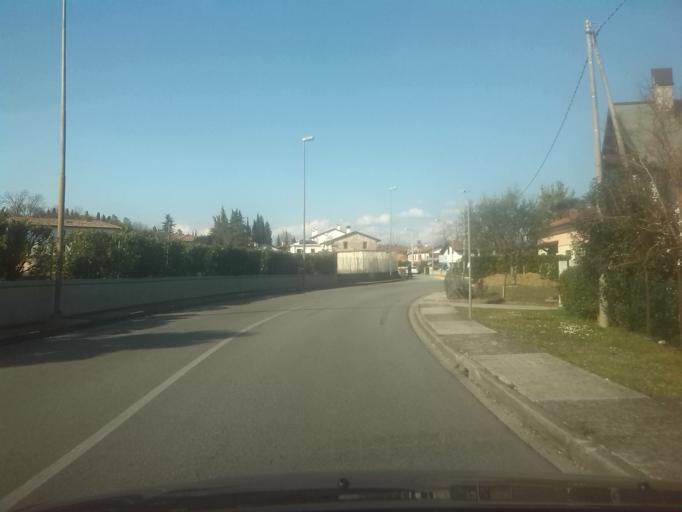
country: IT
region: Friuli Venezia Giulia
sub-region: Provincia di Udine
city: Manzano
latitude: 45.9886
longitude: 13.3901
